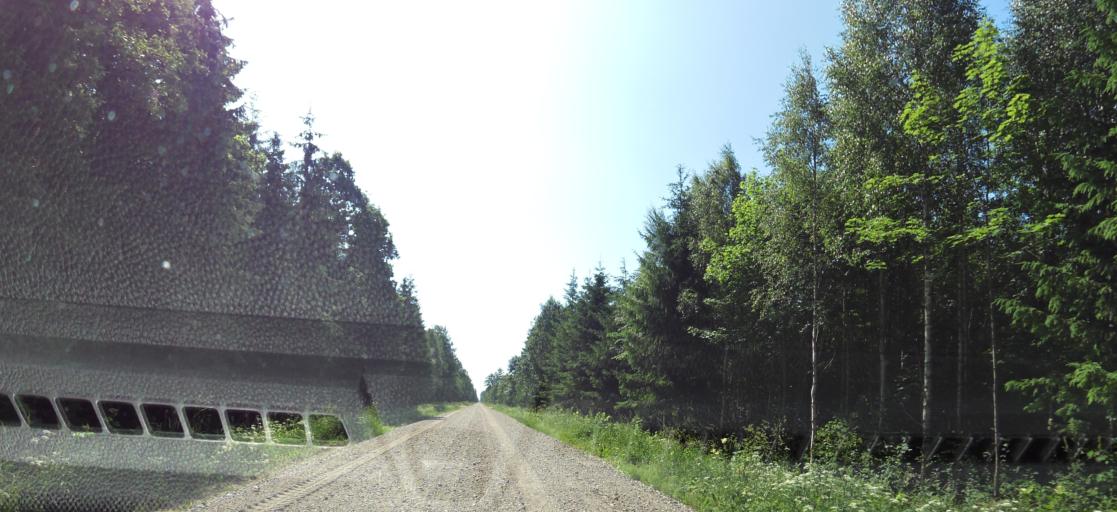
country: LT
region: Panevezys
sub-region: Birzai
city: Birzai
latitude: 56.2319
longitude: 24.9910
